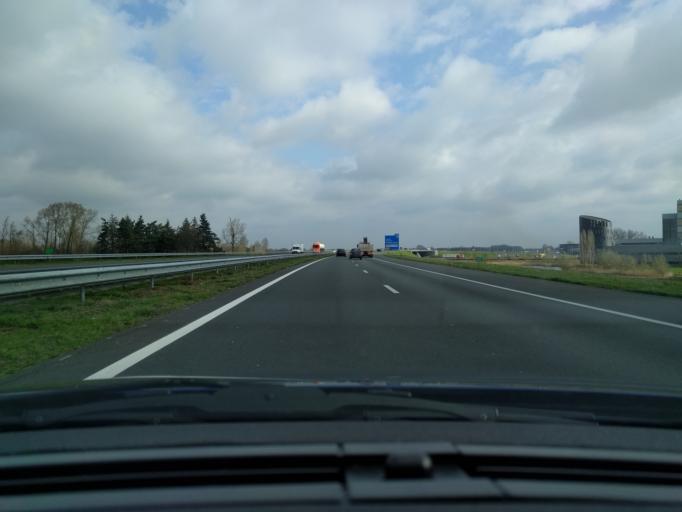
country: NL
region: North Brabant
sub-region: Gemeente Veghel
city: Eerde
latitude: 51.6195
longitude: 5.5019
